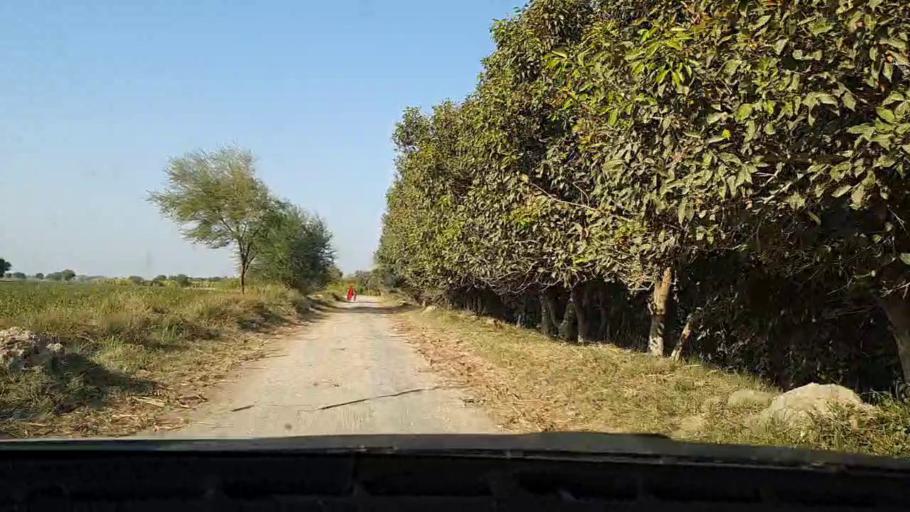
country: PK
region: Sindh
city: Tando Mittha Khan
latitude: 25.8526
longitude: 69.3328
